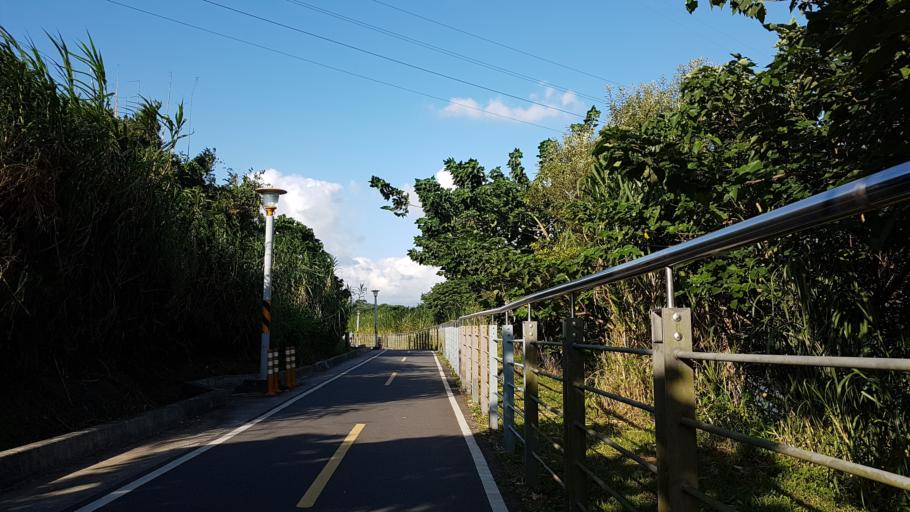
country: TW
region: Taipei
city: Taipei
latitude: 25.0014
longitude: 121.5310
